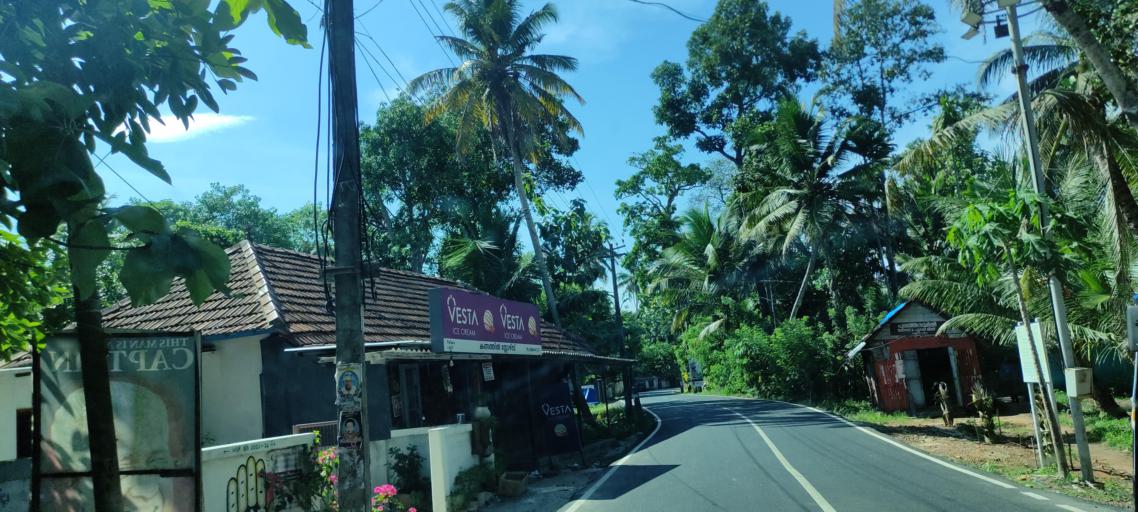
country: IN
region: Kerala
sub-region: Alappuzha
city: Kayankulam
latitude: 9.3052
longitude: 76.3863
